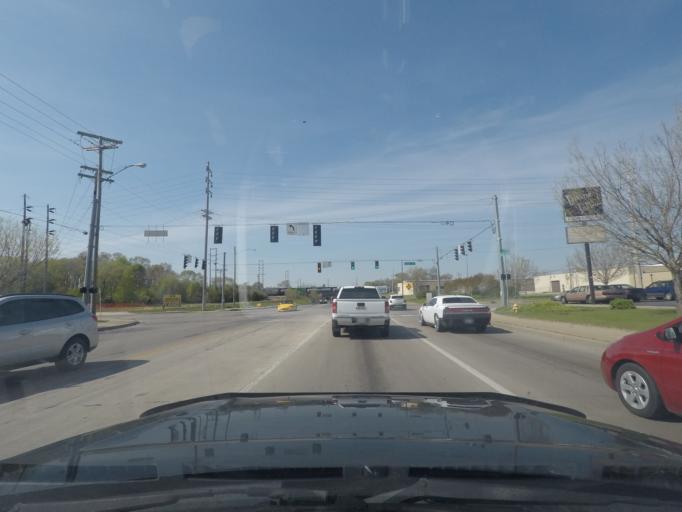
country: US
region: Indiana
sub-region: Elkhart County
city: Elkhart
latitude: 41.6666
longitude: -86.0032
